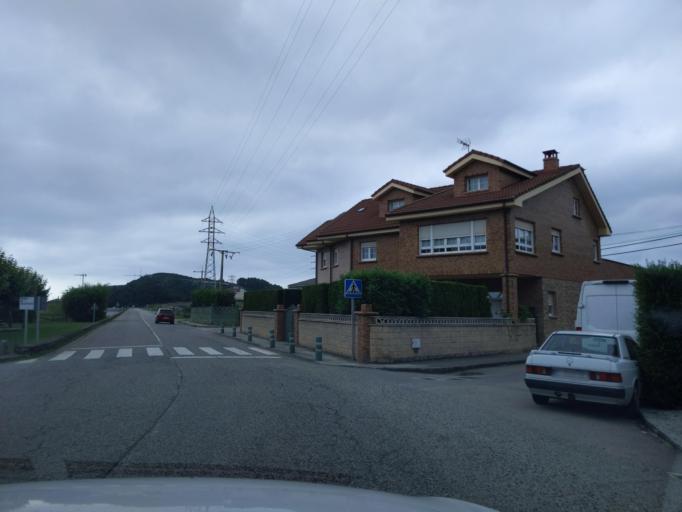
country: ES
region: Asturias
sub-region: Province of Asturias
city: Aviles
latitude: 43.5900
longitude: -5.9134
